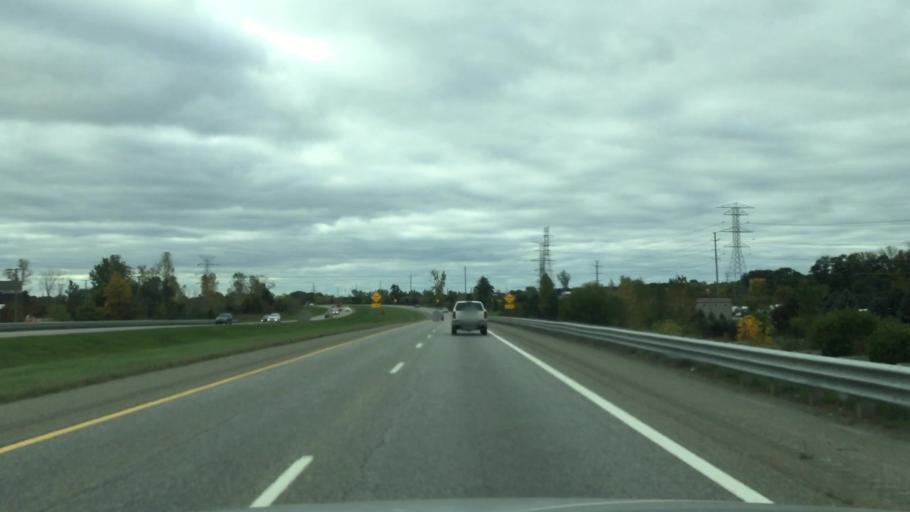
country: US
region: Michigan
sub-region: Macomb County
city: Romeo
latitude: 42.7850
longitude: -83.0068
